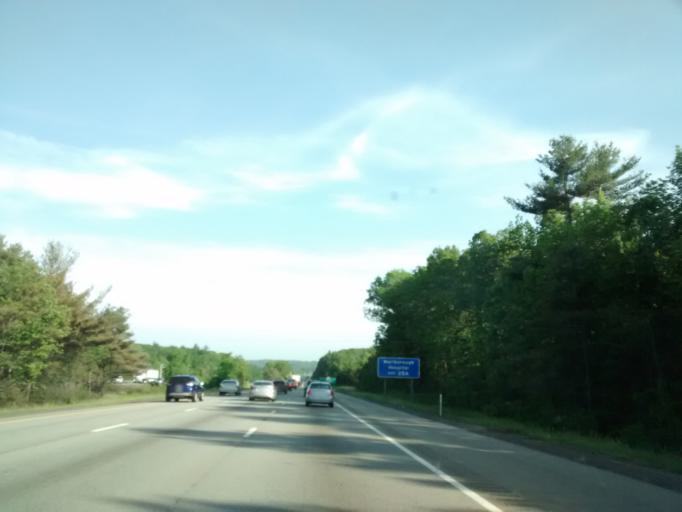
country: US
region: Massachusetts
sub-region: Worcester County
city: Berlin
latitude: 42.3875
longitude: -71.6048
